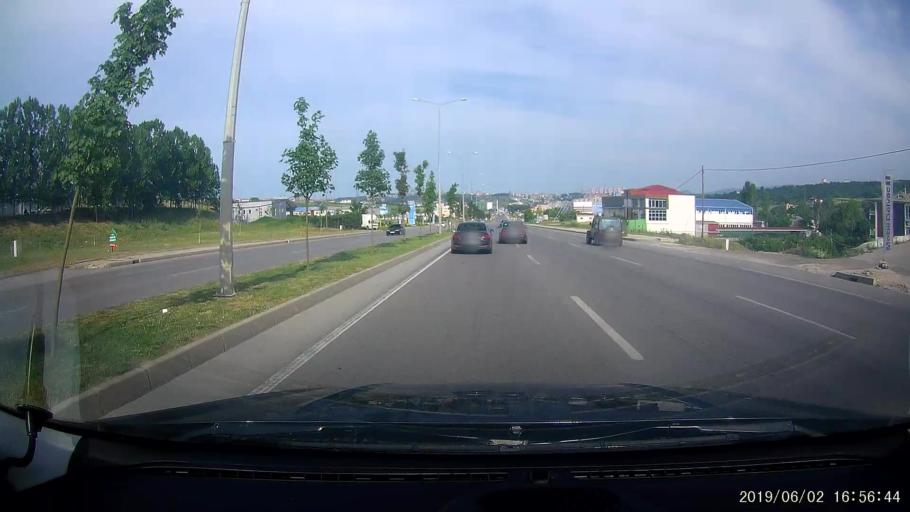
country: TR
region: Samsun
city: Samsun
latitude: 41.2920
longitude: 36.2645
